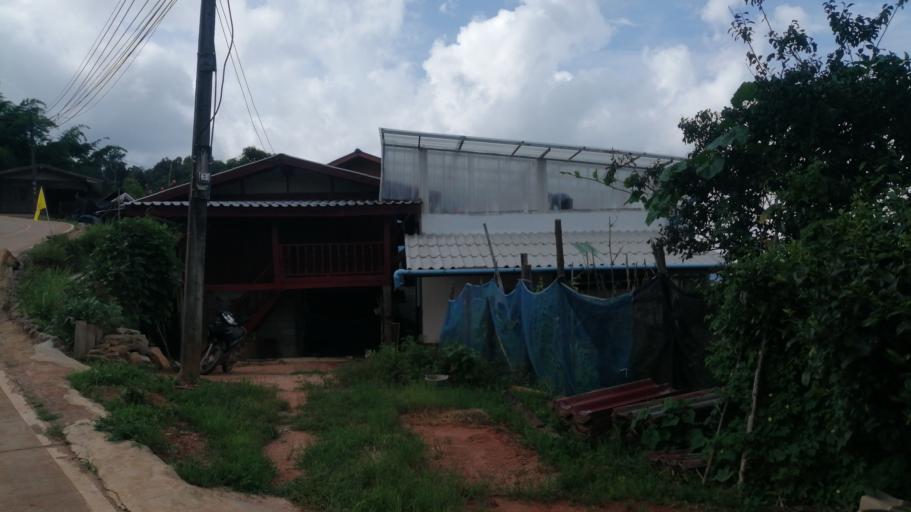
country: TH
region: Chiang Mai
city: Phrao
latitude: 19.5100
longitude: 99.3392
